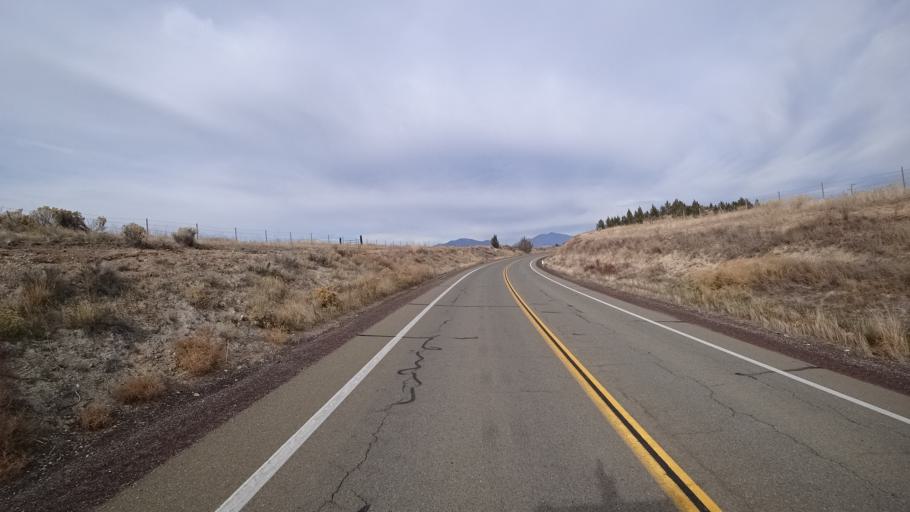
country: US
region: California
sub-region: Siskiyou County
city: Montague
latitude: 41.7014
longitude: -122.5390
